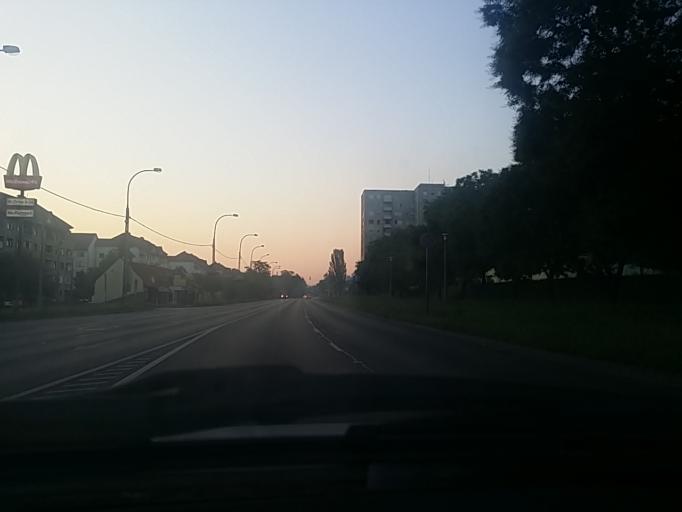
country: HU
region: Budapest
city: Budapest XVII. keruelet
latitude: 47.4838
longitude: 19.2357
